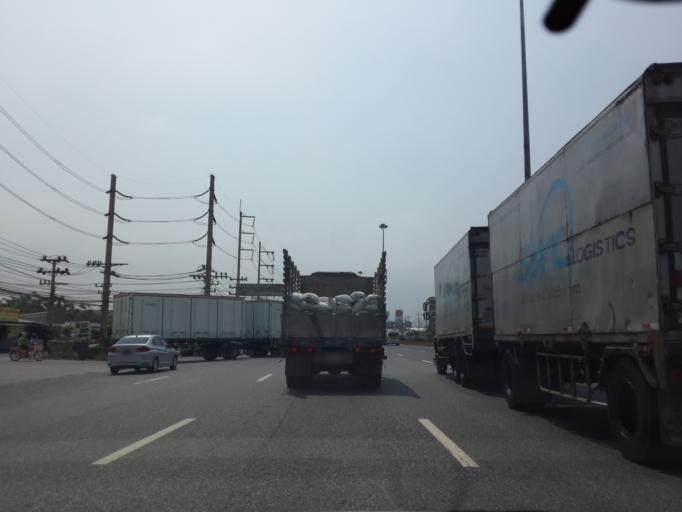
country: TH
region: Chon Buri
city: Chon Buri
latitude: 13.4169
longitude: 100.9982
